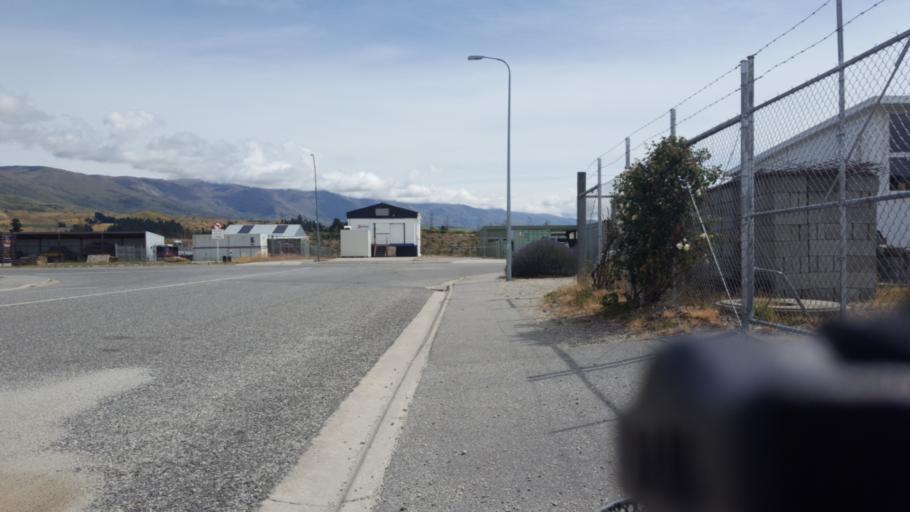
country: NZ
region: Otago
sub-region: Queenstown-Lakes District
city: Wanaka
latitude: -45.0501
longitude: 169.1917
